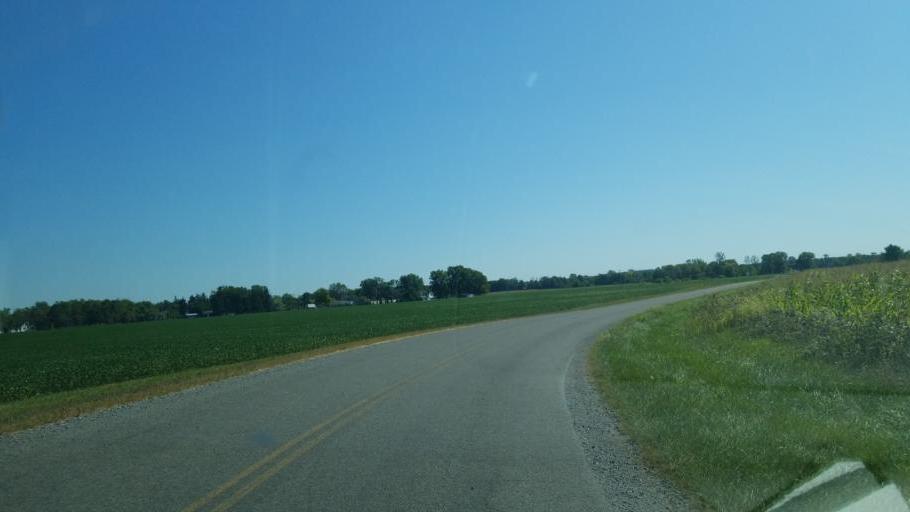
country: US
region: Ohio
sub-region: Logan County
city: Northwood
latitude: 40.5153
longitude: -83.7635
